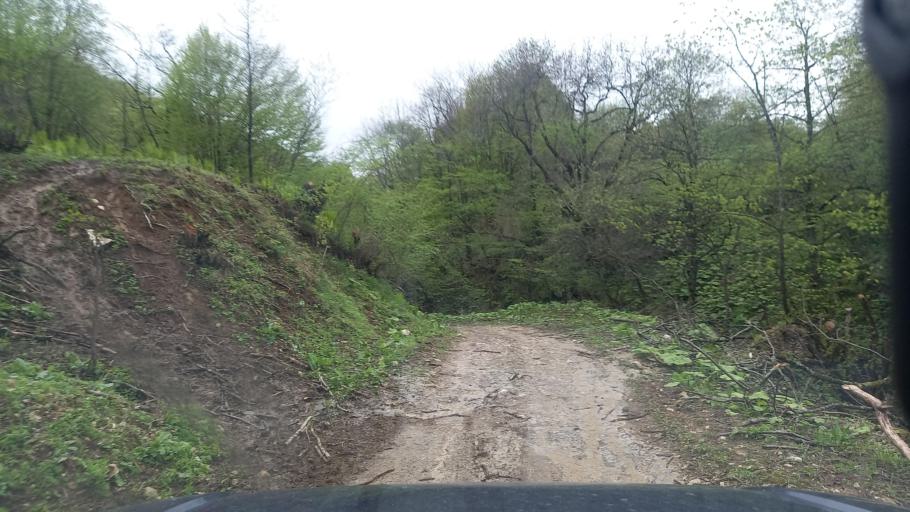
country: RU
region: Kabardino-Balkariya
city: Babugent
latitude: 43.2121
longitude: 43.5461
